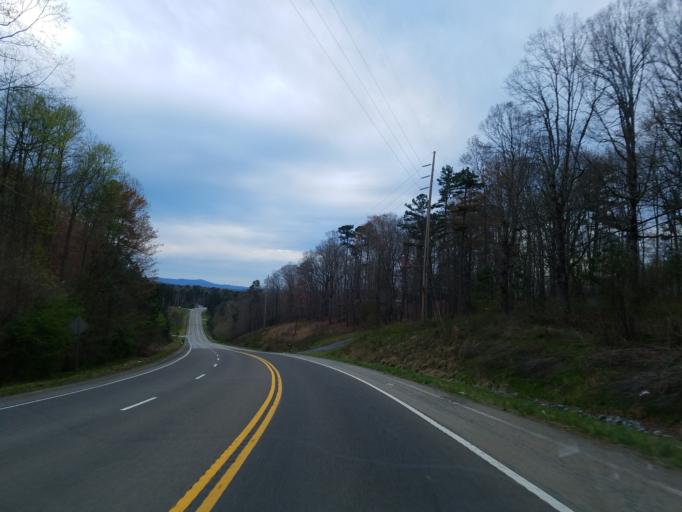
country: US
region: Georgia
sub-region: Gilmer County
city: Ellijay
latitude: 34.6554
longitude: -84.4382
